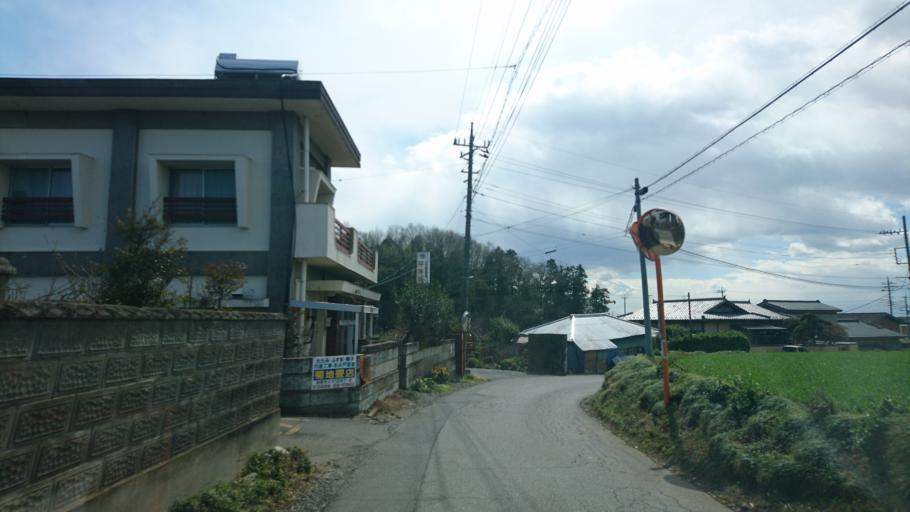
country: JP
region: Ibaraki
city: Yuki
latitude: 36.2750
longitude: 139.9084
